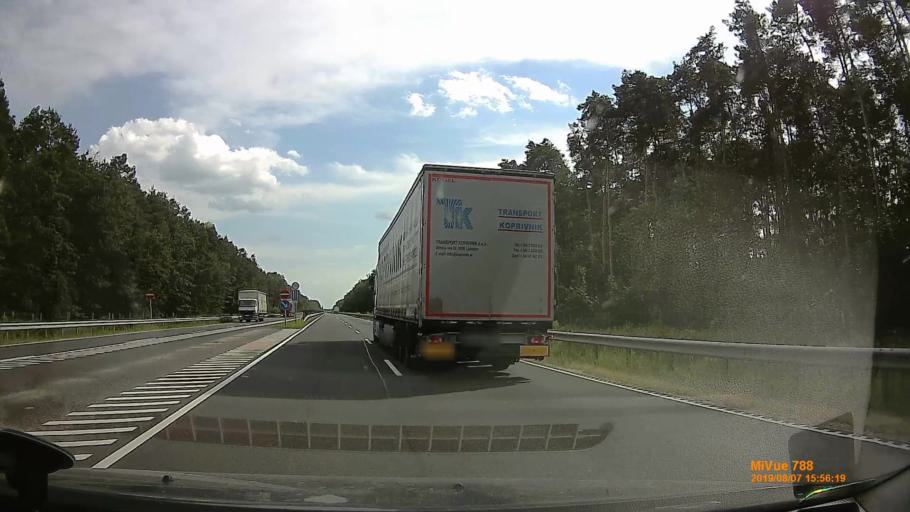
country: HU
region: Vas
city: Kormend
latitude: 47.0624
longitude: 16.6163
